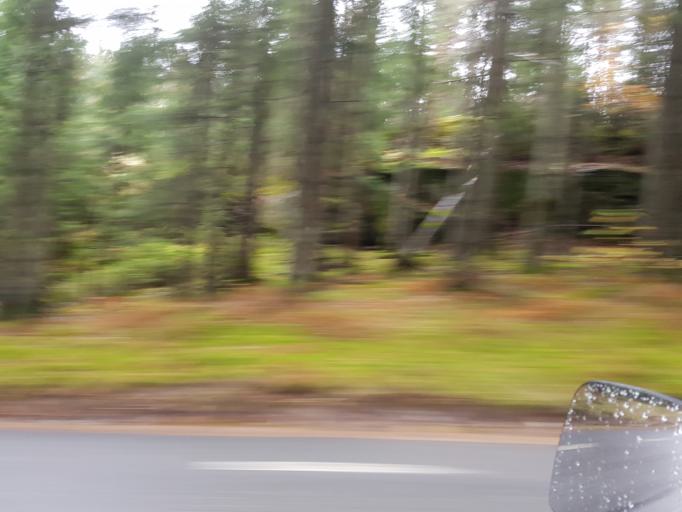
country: SE
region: Vaestra Goetaland
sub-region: Orust
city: Henan
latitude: 58.2741
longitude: 11.7215
